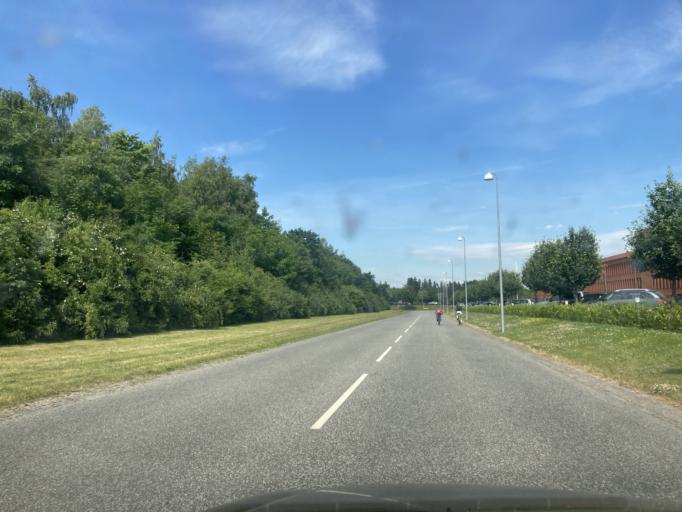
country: DK
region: Capital Region
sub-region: Hillerod Kommune
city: Nodebo
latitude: 55.9345
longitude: 12.3551
